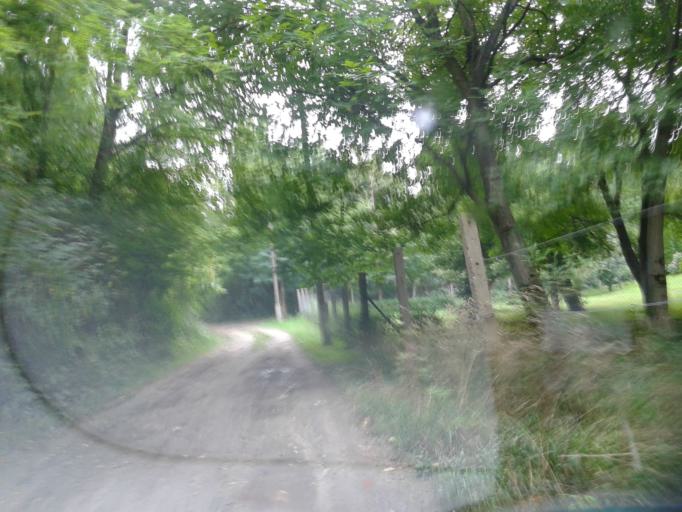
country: HU
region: Bacs-Kiskun
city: Dunapataj
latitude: 46.6761
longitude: 18.9976
